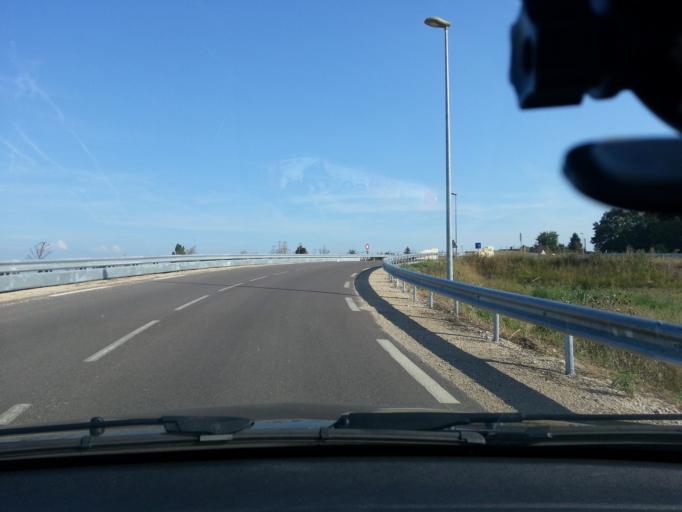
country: FR
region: Bourgogne
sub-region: Departement de Saone-et-Loire
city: Saint-Remy
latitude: 46.7563
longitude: 4.8156
